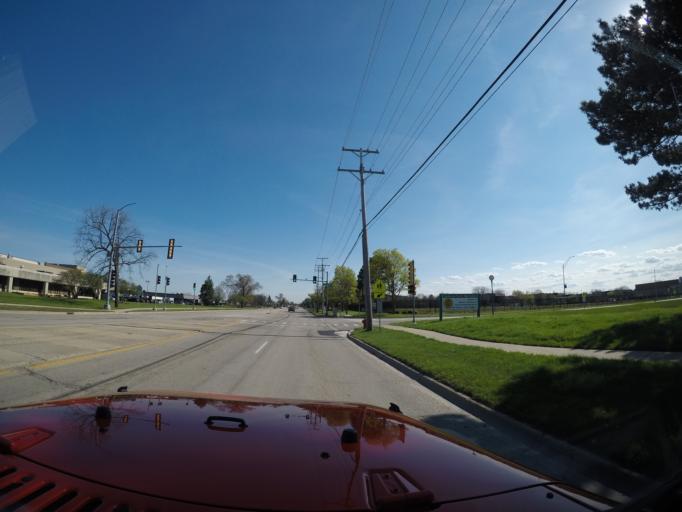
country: US
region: Illinois
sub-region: Cook County
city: Northbrook
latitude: 42.1104
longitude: -87.8295
